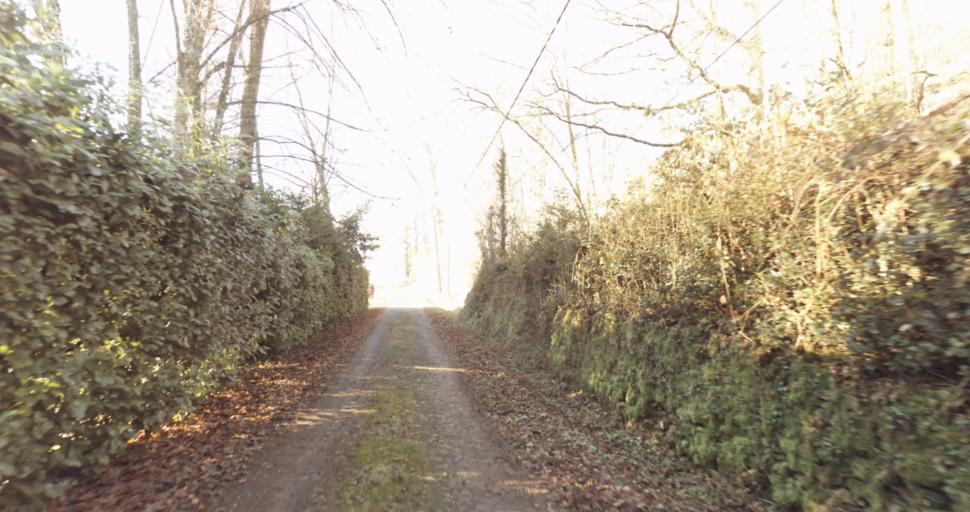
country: FR
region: Limousin
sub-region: Departement de la Haute-Vienne
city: Aixe-sur-Vienne
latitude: 45.8007
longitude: 1.1577
